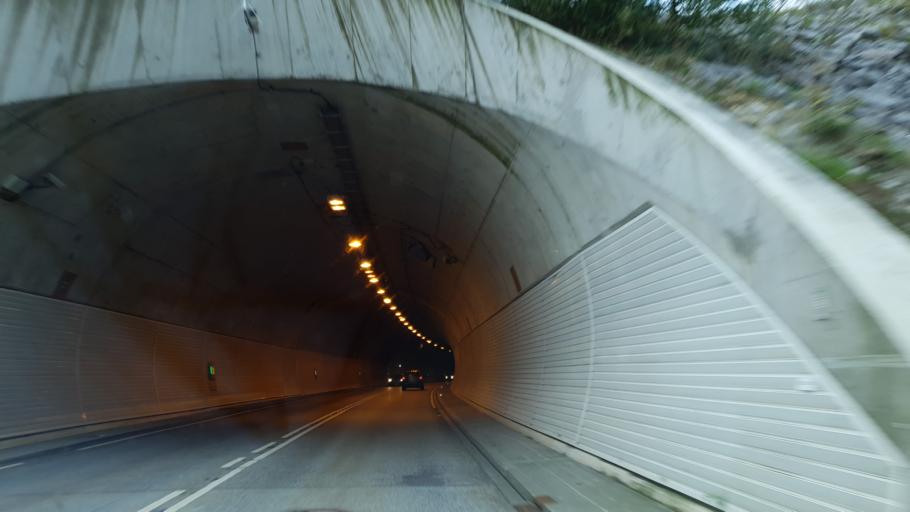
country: DE
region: Baden-Wuerttemberg
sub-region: Tuebingen Region
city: Isny im Allgau
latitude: 47.6845
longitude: 10.0274
